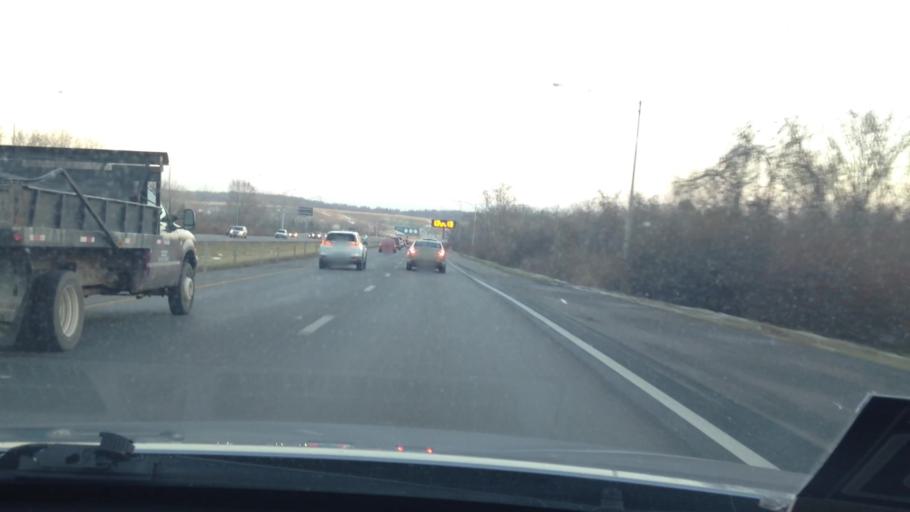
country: US
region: Kansas
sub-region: Johnson County
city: Leawood
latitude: 38.9834
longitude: -94.5506
